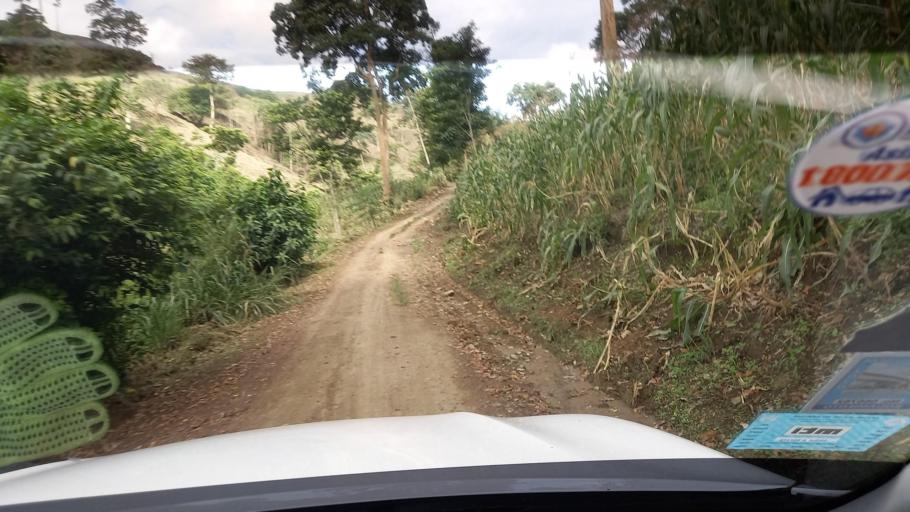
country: NI
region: Jinotega
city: San Jose de Bocay
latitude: 13.4004
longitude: -85.6989
